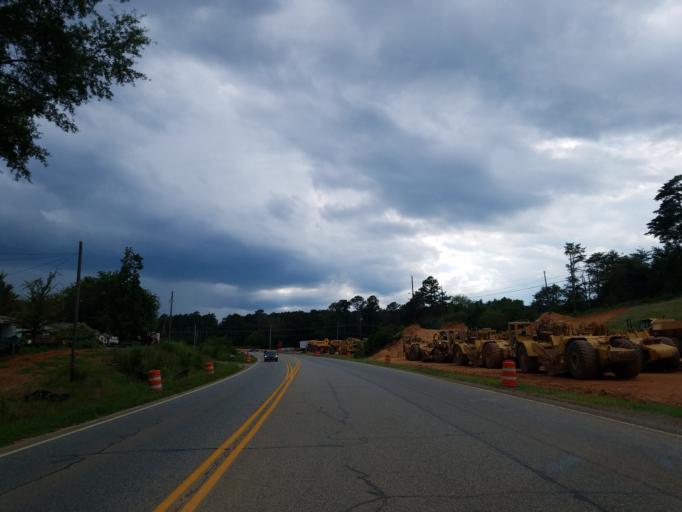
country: US
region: Georgia
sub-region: Bartow County
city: Adairsville
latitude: 34.3743
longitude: -84.9854
